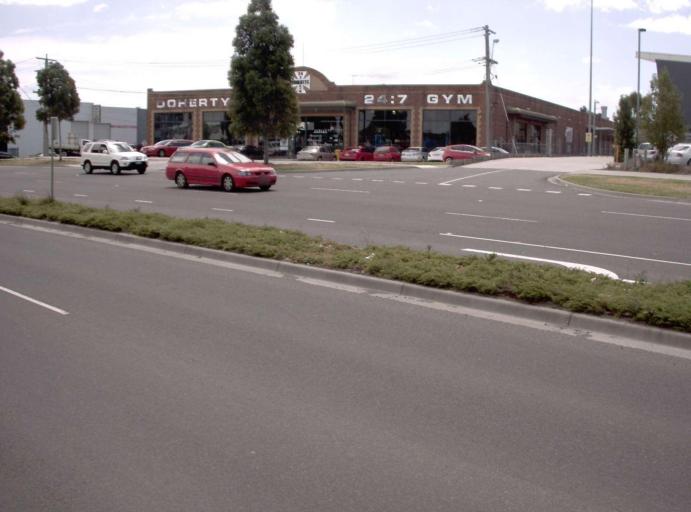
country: AU
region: Victoria
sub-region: Greater Dandenong
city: Dandenong
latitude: -37.9898
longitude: 145.2041
